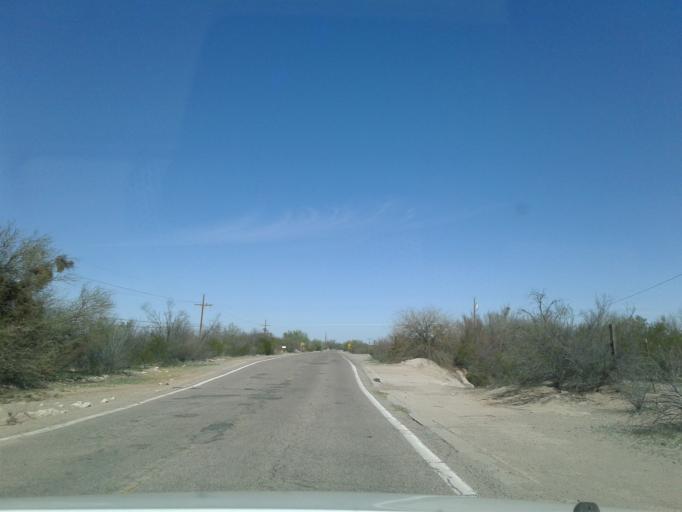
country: US
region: Arizona
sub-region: Pima County
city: Avra Valley
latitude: 32.4372
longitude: -111.3470
